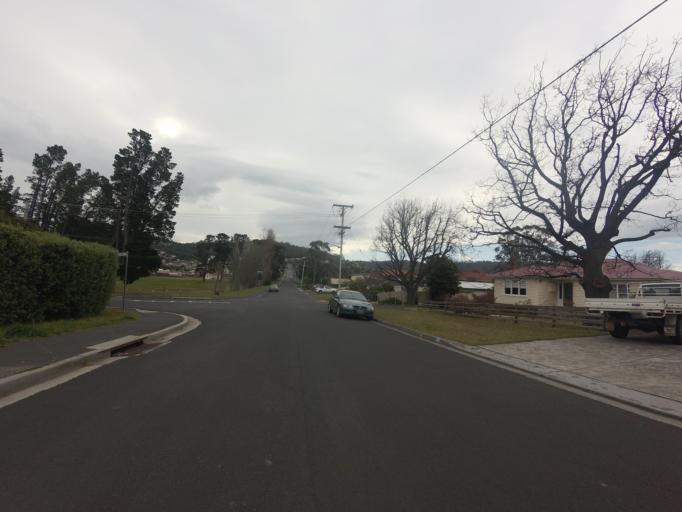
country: AU
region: Tasmania
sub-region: Clarence
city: Bellerive
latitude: -42.8804
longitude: 147.3871
